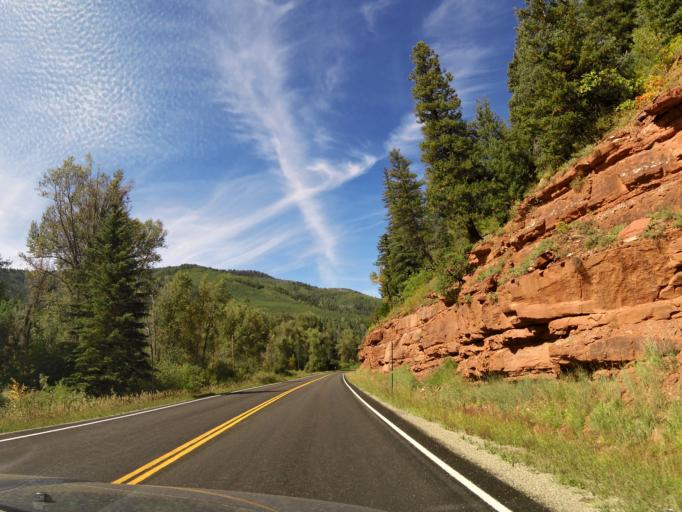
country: US
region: Colorado
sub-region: Montezuma County
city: Mancos
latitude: 37.5763
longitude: -108.1828
